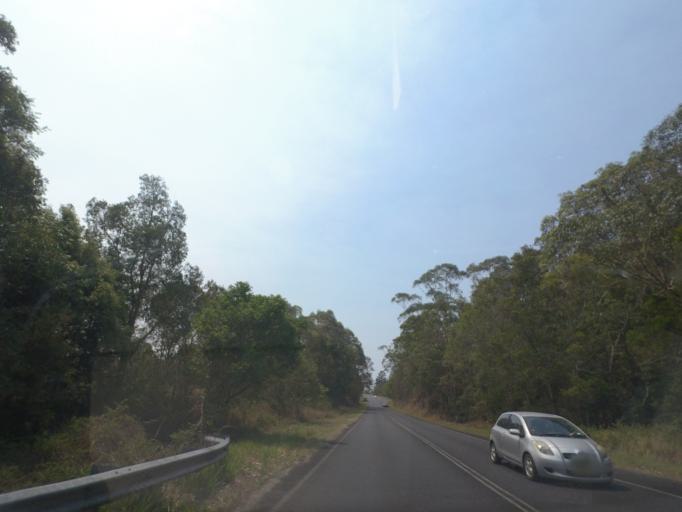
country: AU
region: New South Wales
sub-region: Byron Shire
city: Brunswick Heads
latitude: -28.4961
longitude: 153.5264
